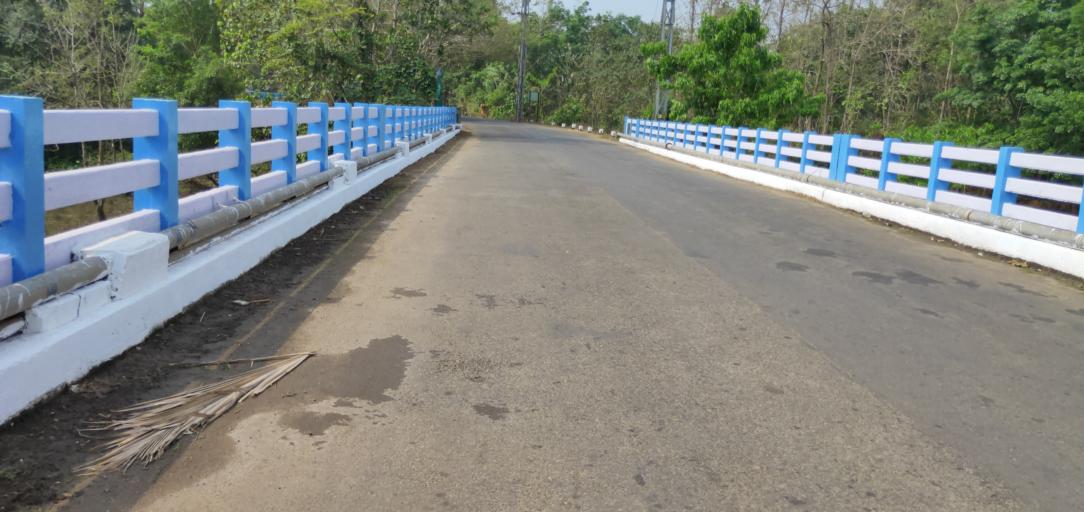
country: IN
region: Kerala
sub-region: Malappuram
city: Manjeri
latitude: 11.2297
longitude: 76.2746
